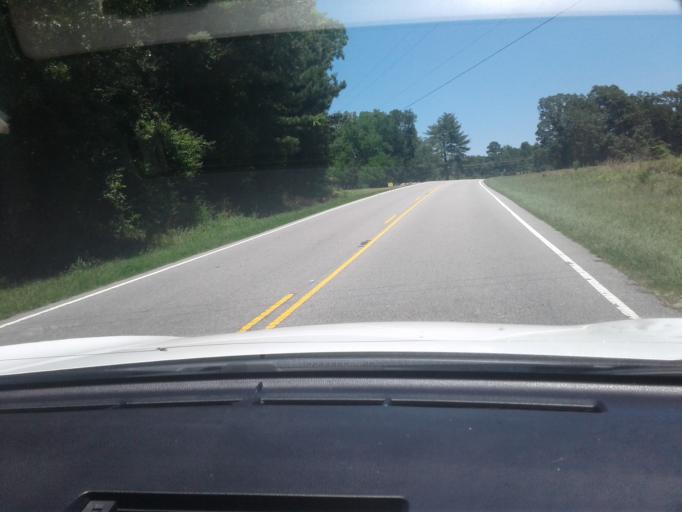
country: US
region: North Carolina
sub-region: Harnett County
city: Lillington
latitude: 35.3664
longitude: -78.8902
